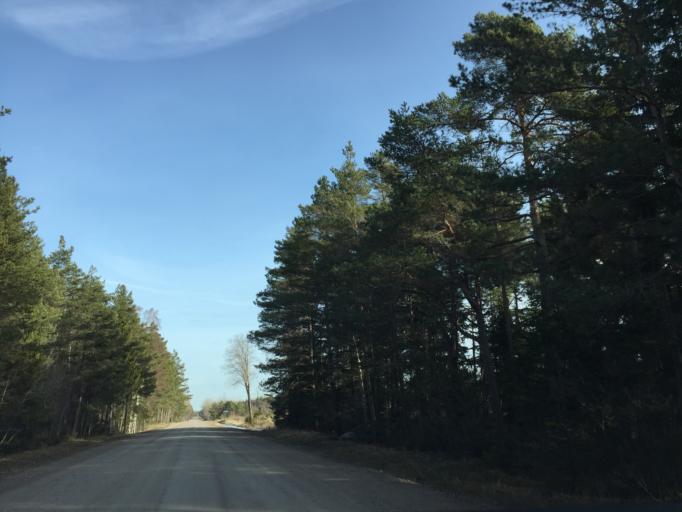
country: EE
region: Saare
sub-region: Kuressaare linn
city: Kuressaare
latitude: 58.3147
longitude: 21.9866
